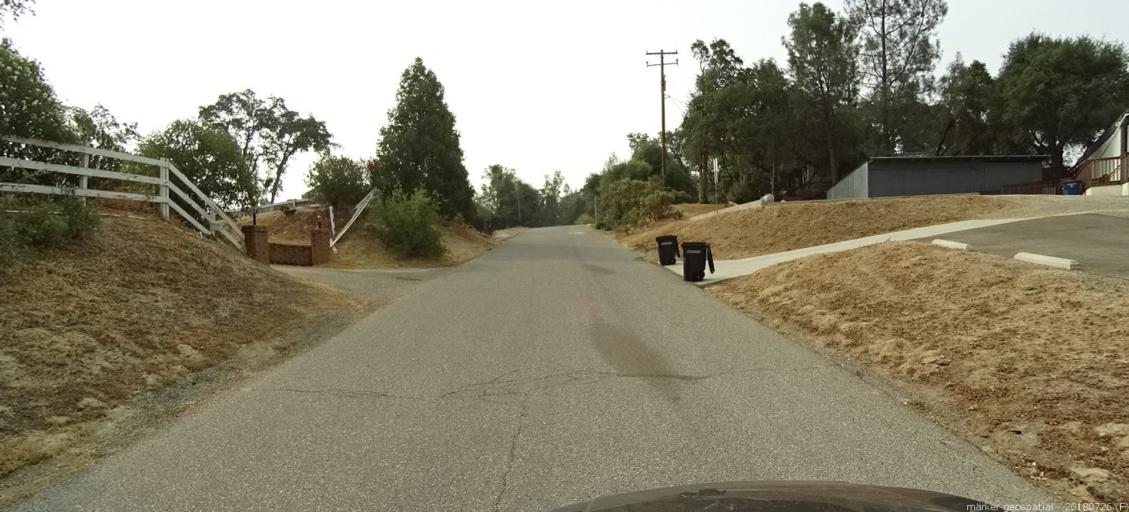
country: US
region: California
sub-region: Madera County
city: Coarsegold
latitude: 37.2187
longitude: -119.7058
